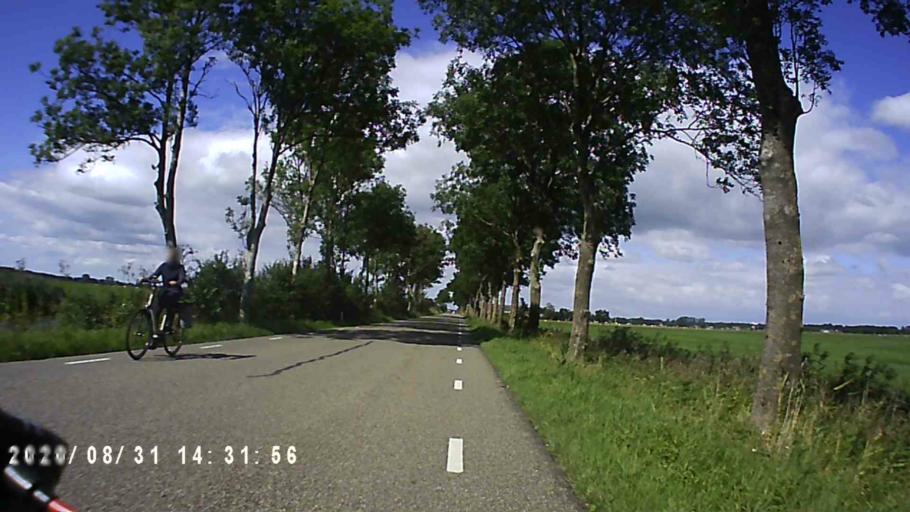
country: NL
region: Groningen
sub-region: Gemeente Zuidhorn
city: Zuidhorn
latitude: 53.2247
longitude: 6.4037
